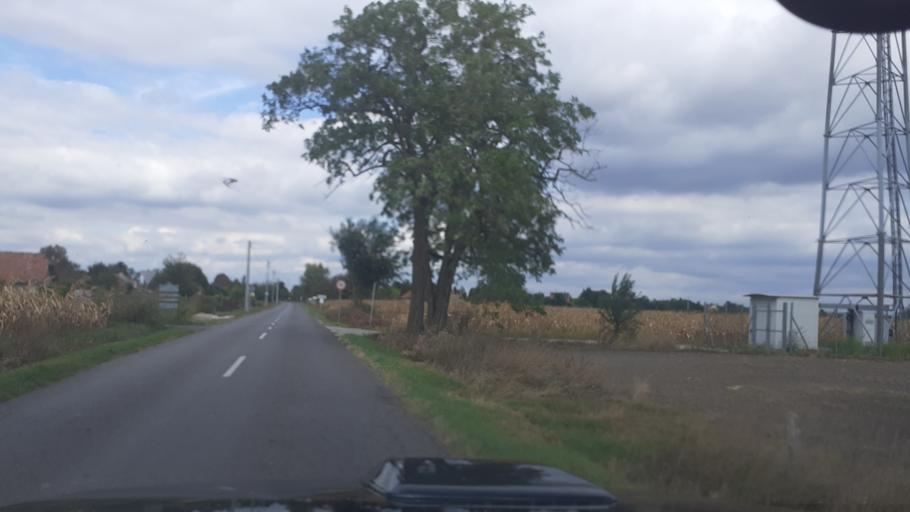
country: HU
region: Bacs-Kiskun
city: Apostag
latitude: 46.8698
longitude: 18.9559
